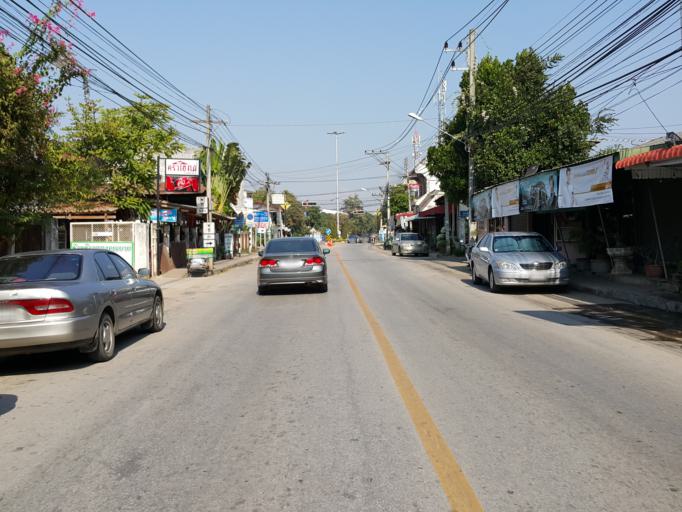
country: TH
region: Lampang
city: Lampang
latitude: 18.2963
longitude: 99.4994
